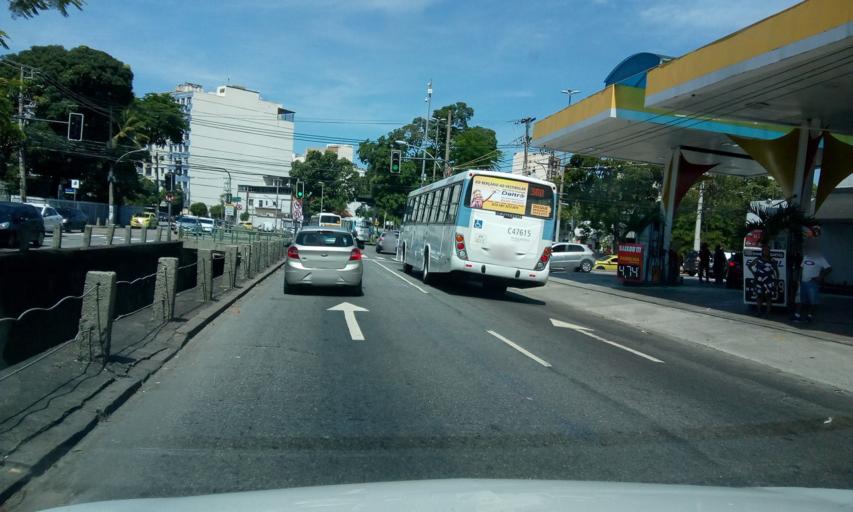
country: BR
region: Rio de Janeiro
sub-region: Rio De Janeiro
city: Rio de Janeiro
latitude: -22.9158
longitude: -43.2360
